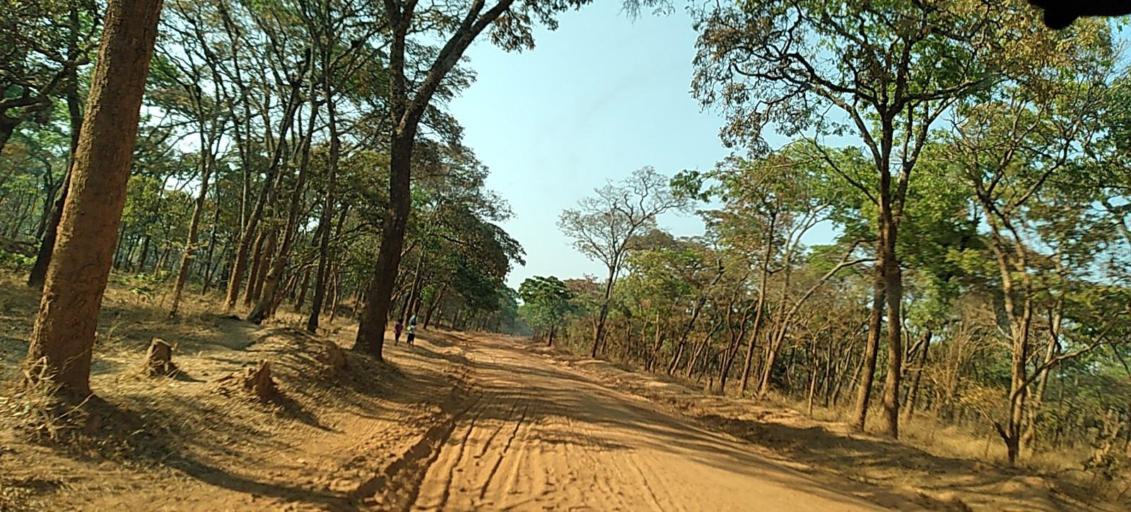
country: ZM
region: North-Western
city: Kasempa
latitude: -13.6065
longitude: 25.9775
